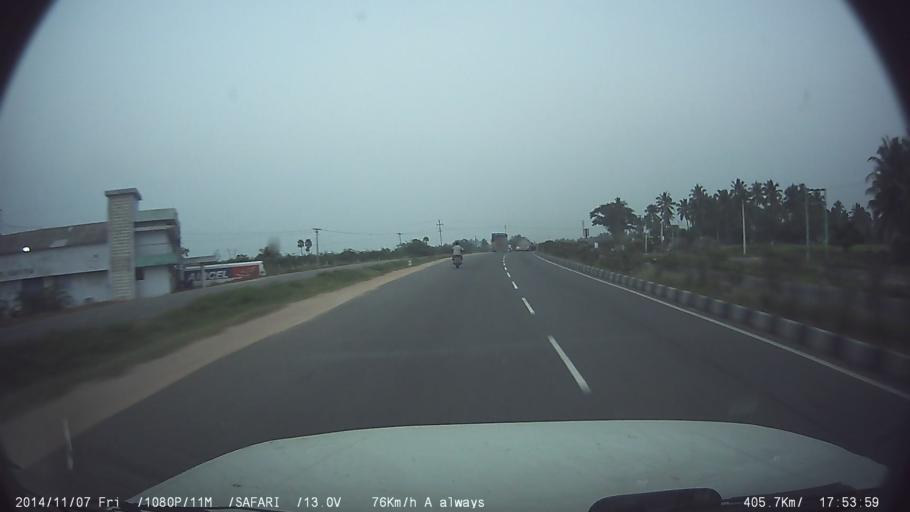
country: IN
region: Tamil Nadu
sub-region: Erode
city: Perundurai
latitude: 11.3070
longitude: 77.6043
